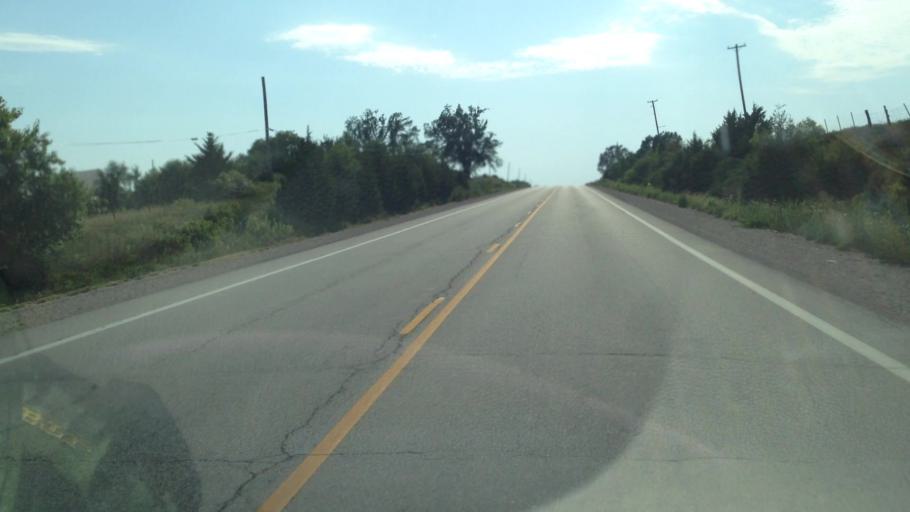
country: US
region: Kansas
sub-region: Anderson County
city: Garnett
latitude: 38.0816
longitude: -95.1796
